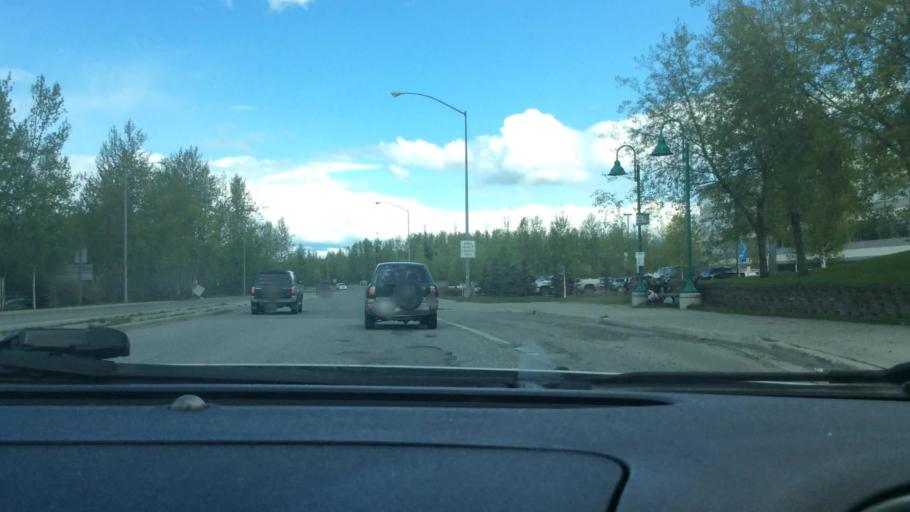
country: US
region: Alaska
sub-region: Anchorage Municipality
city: Anchorage
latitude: 61.1811
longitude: -149.8081
